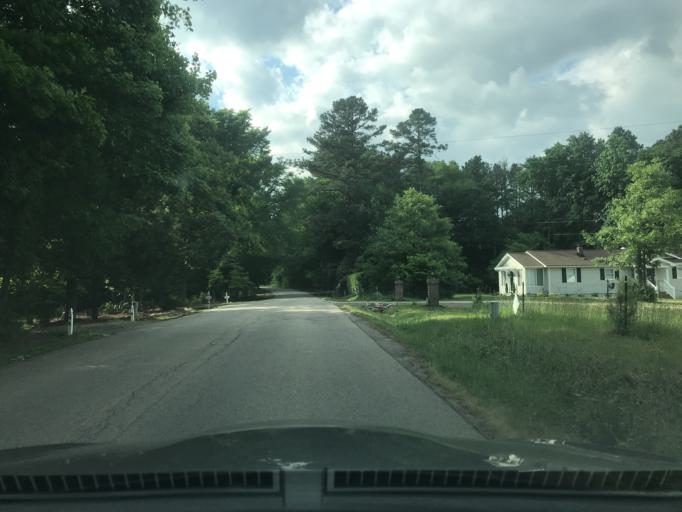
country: US
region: North Carolina
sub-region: Wake County
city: Wake Forest
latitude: 35.9219
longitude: -78.5727
